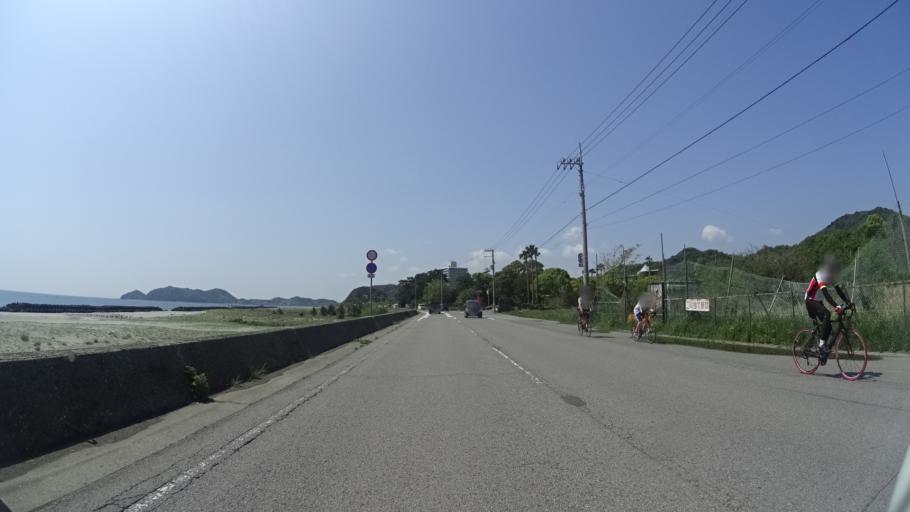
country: JP
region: Tokushima
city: Narutocho-mitsuishi
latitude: 34.2023
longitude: 134.6256
